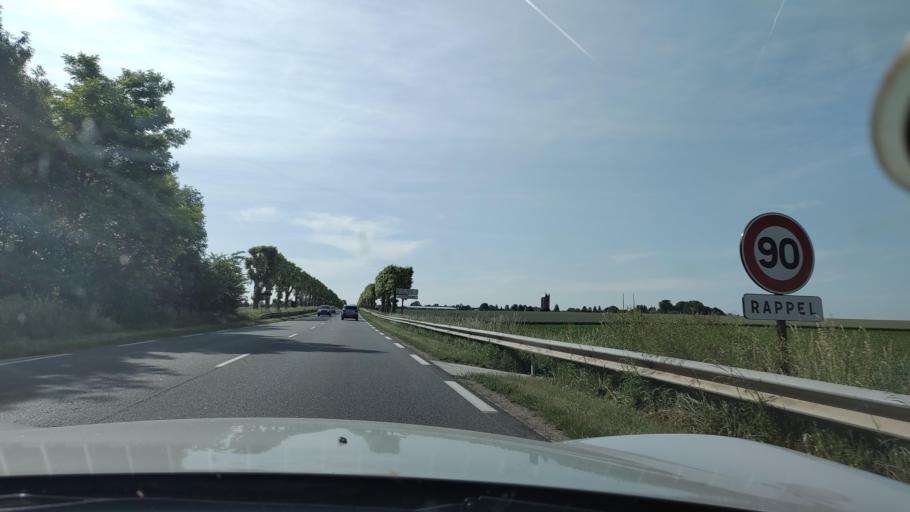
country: FR
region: Ile-de-France
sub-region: Departement de Seine-et-Marne
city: Sourdun
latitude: 48.5445
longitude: 3.3400
